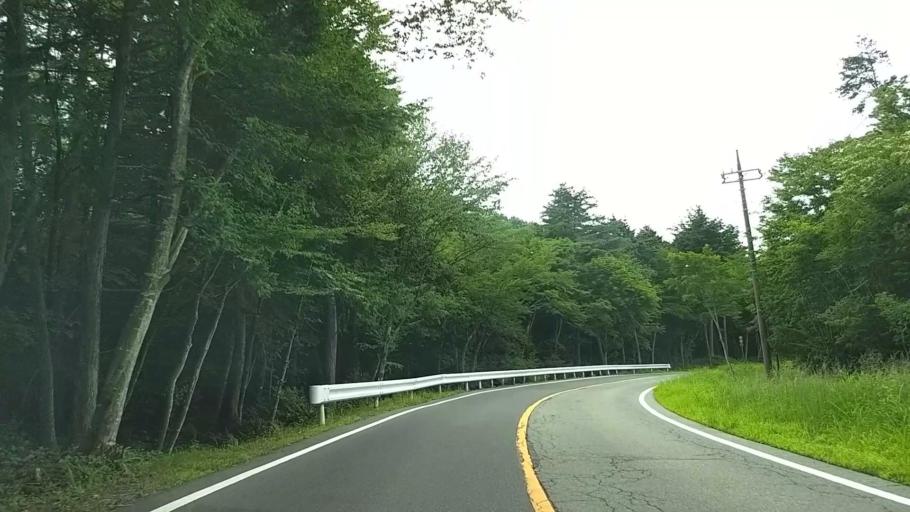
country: JP
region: Yamanashi
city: Fujikawaguchiko
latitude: 35.4880
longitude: 138.6684
